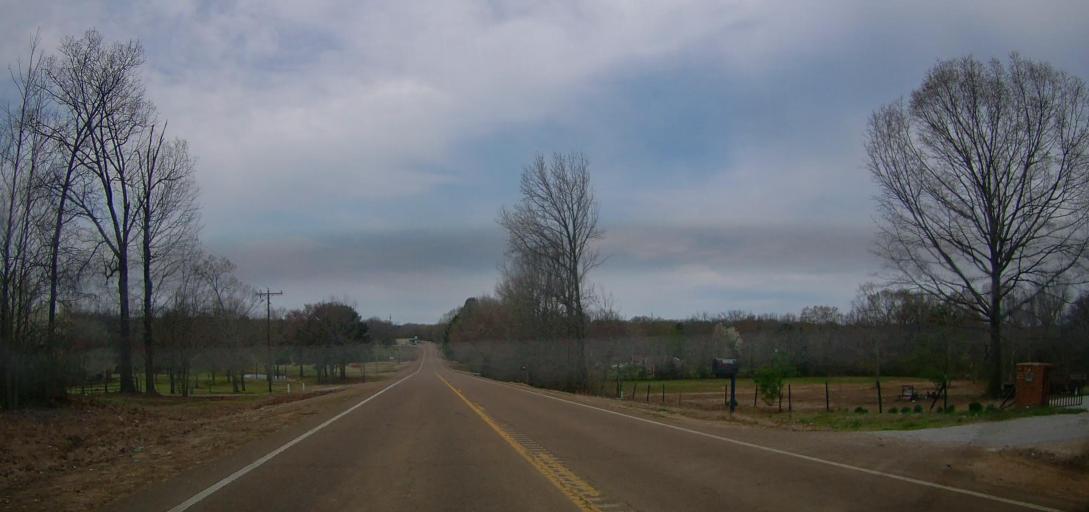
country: US
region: Mississippi
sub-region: Marshall County
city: Byhalia
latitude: 34.8442
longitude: -89.6118
